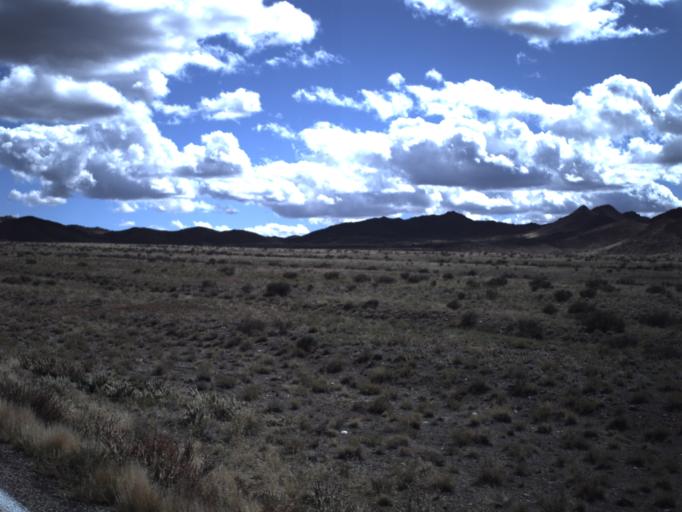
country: US
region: Utah
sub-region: Beaver County
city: Milford
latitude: 38.4424
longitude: -113.3217
